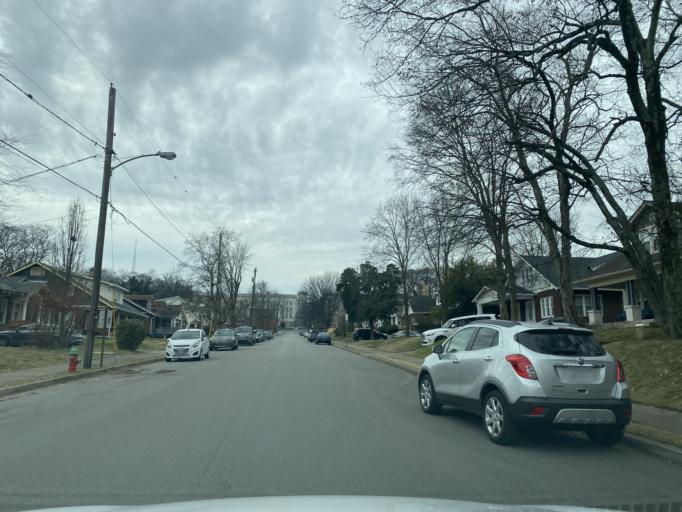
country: US
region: Tennessee
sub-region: Davidson County
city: Nashville
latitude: 36.1389
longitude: -86.7927
